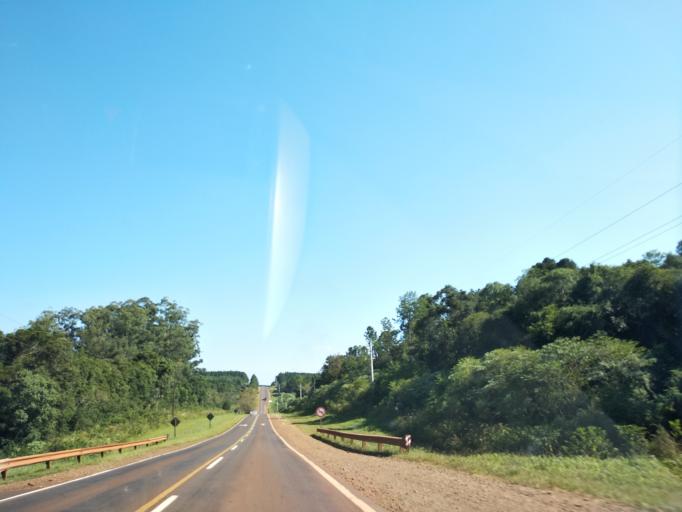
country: AR
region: Misiones
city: Capiovi
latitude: -26.8923
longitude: -55.0563
